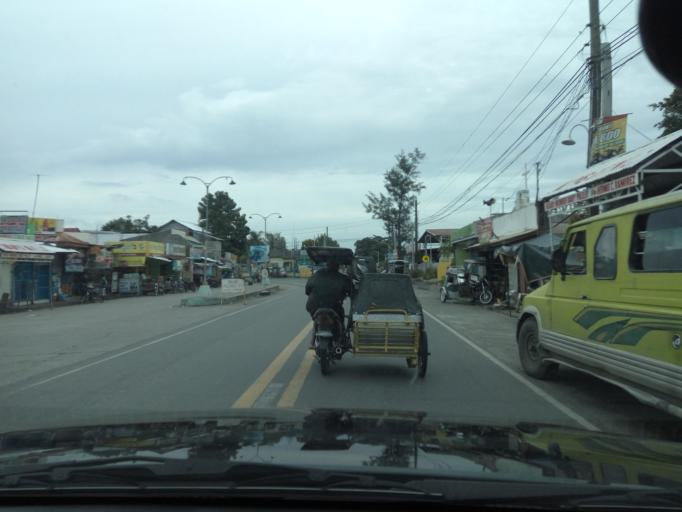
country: PH
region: Central Luzon
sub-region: Province of Nueva Ecija
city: Carmen
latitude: 15.4461
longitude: 120.8263
